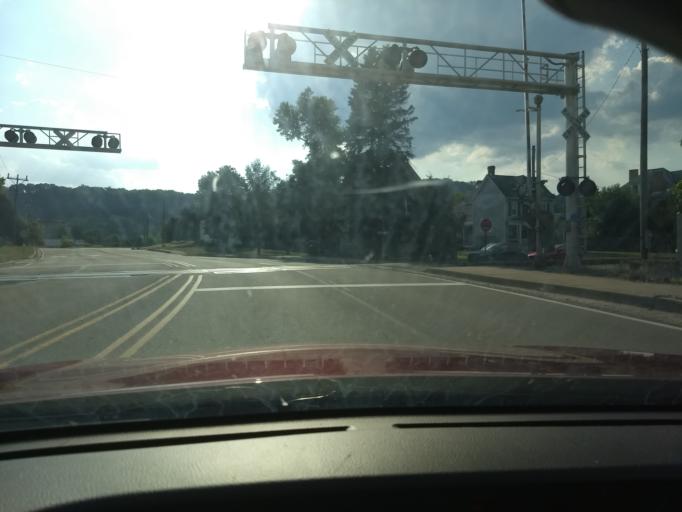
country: US
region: Pennsylvania
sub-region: Westmoreland County
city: Lower Burrell
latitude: 40.5534
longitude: -79.7609
